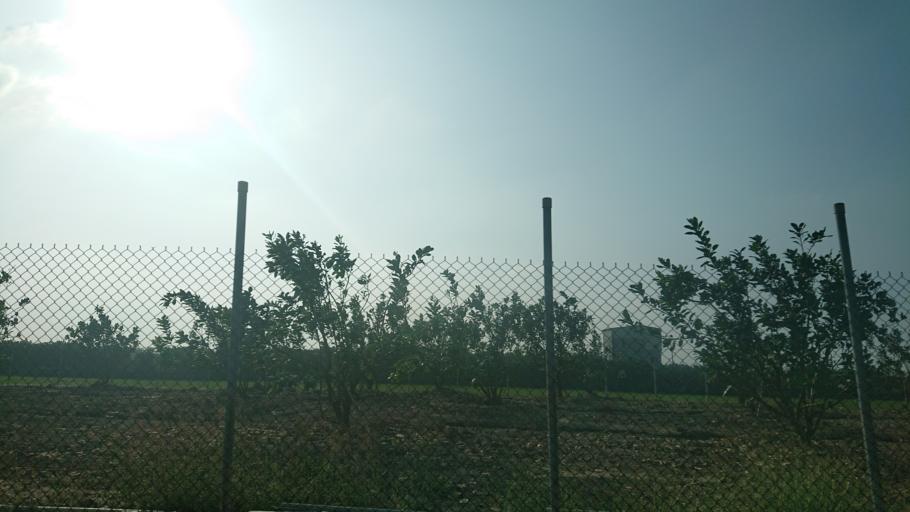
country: TW
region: Taiwan
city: Xinying
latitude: 23.2013
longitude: 120.2713
